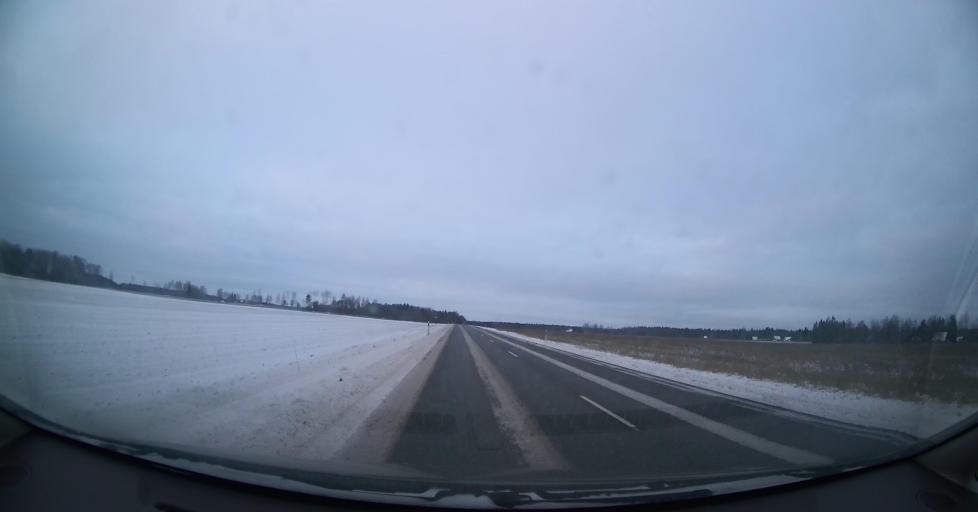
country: EE
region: Harju
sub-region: Anija vald
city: Kehra
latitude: 59.2820
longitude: 25.3701
